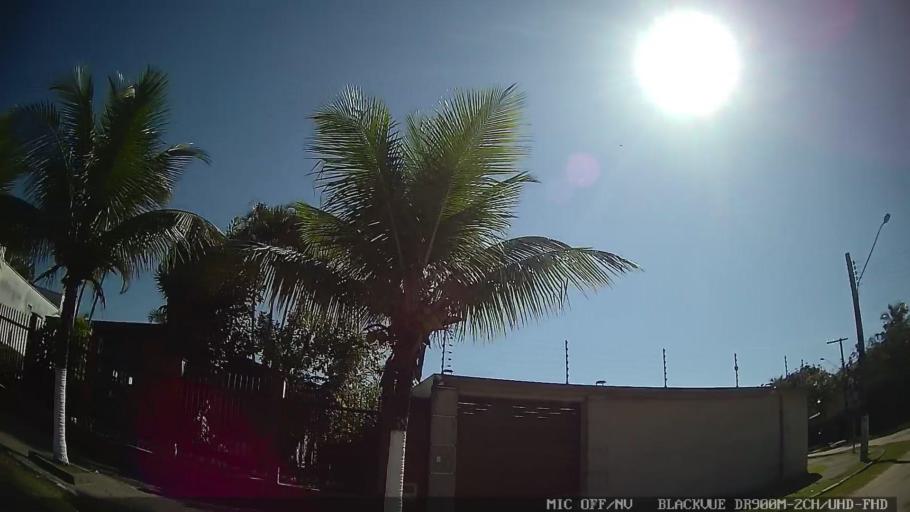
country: BR
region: Sao Paulo
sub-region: Guaruja
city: Guaruja
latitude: -23.9822
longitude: -46.2116
